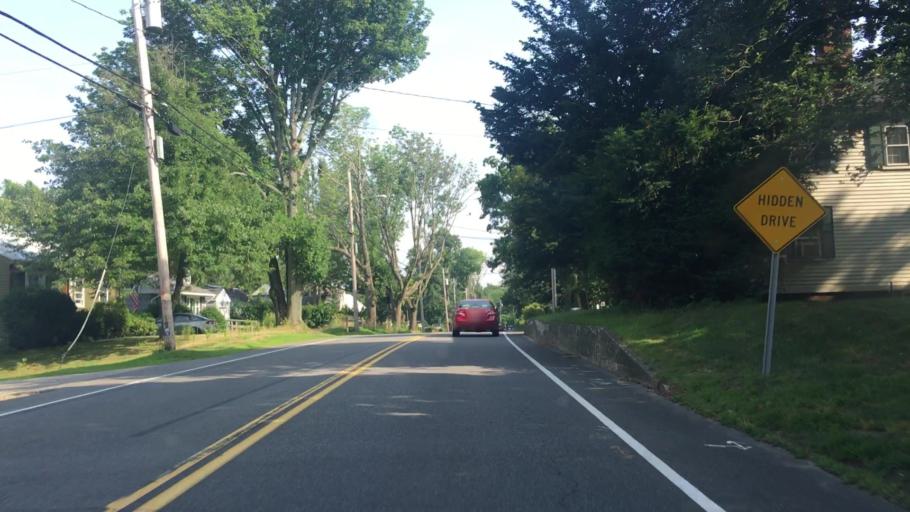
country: US
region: Maine
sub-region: York County
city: Kittery
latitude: 43.0989
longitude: -70.7394
